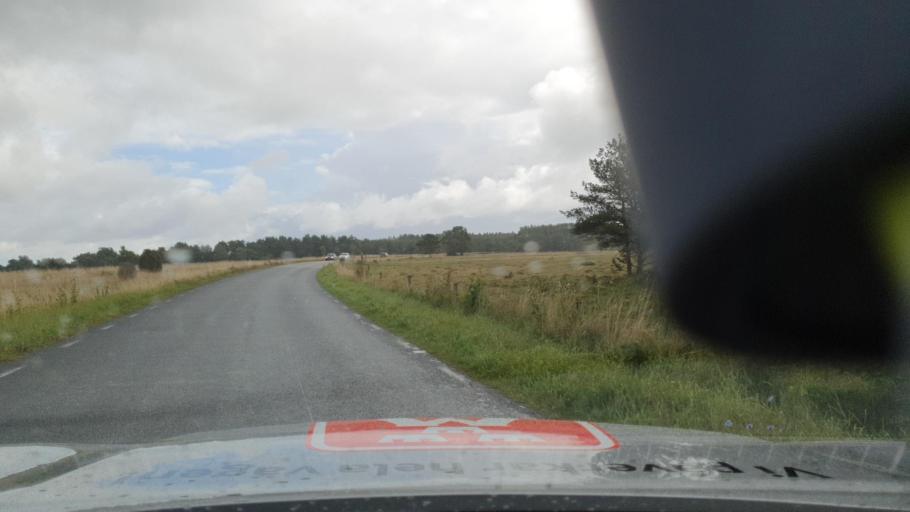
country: SE
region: Gotland
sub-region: Gotland
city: Hemse
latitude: 56.9999
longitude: 18.3106
